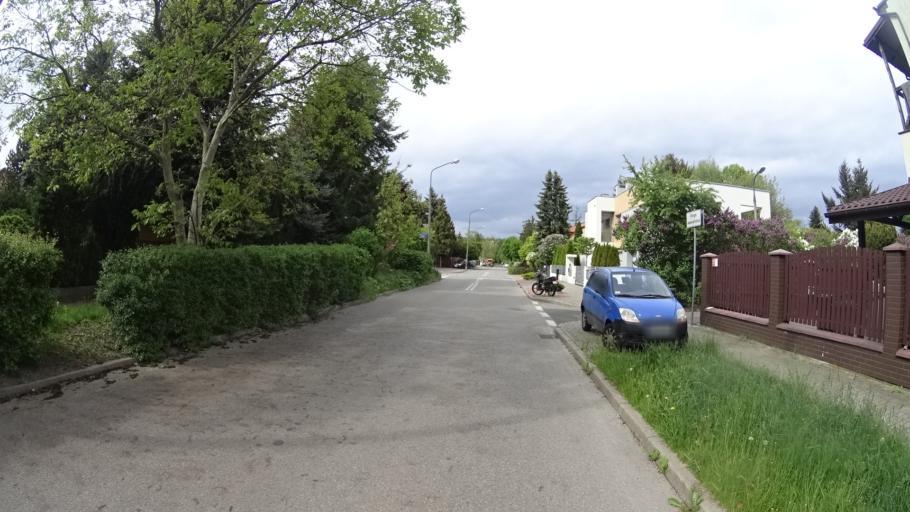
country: PL
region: Masovian Voivodeship
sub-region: Powiat warszawski zachodni
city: Babice
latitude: 52.2496
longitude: 20.8762
